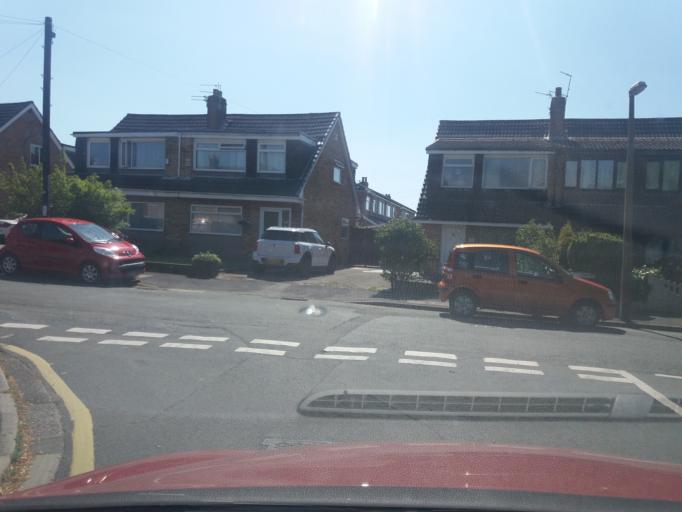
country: GB
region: England
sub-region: Lancashire
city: Preston
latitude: 53.7944
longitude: -2.7044
